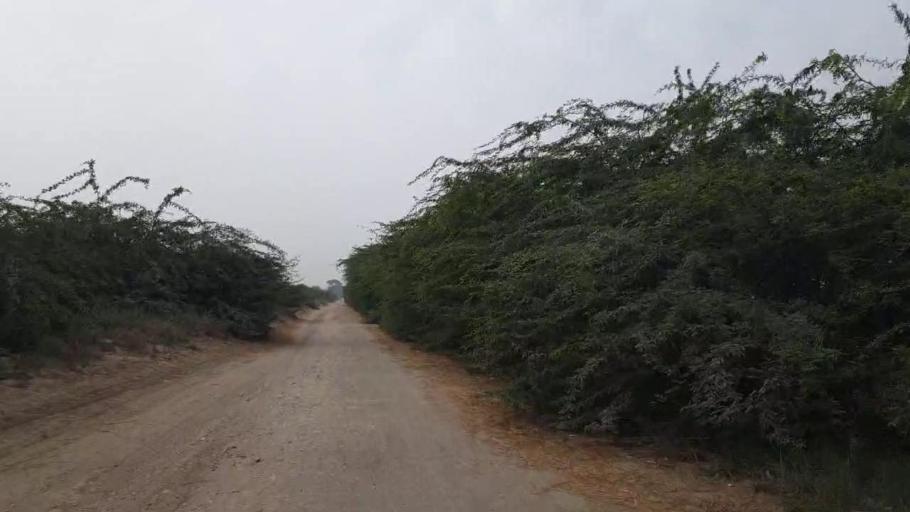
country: PK
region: Sindh
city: Kario
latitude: 24.9135
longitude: 68.5403
